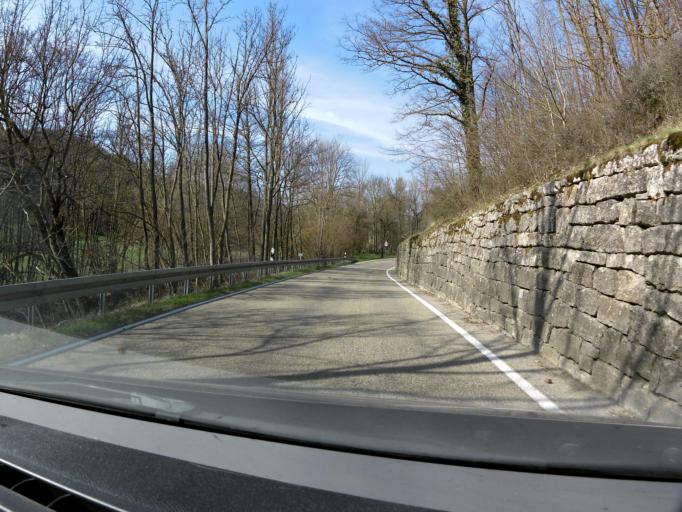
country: DE
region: Bavaria
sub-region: Regierungsbezirk Mittelfranken
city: Adelshofen
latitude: 49.4012
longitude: 10.1579
